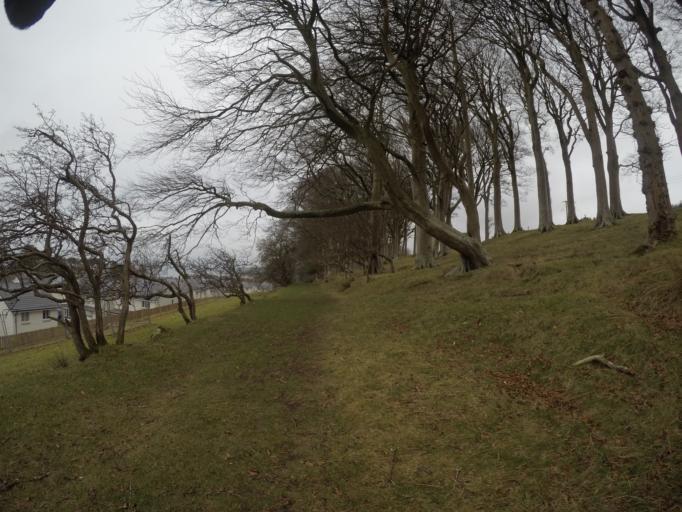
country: GB
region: Scotland
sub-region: North Ayrshire
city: Fairlie
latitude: 55.7586
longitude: -4.8496
